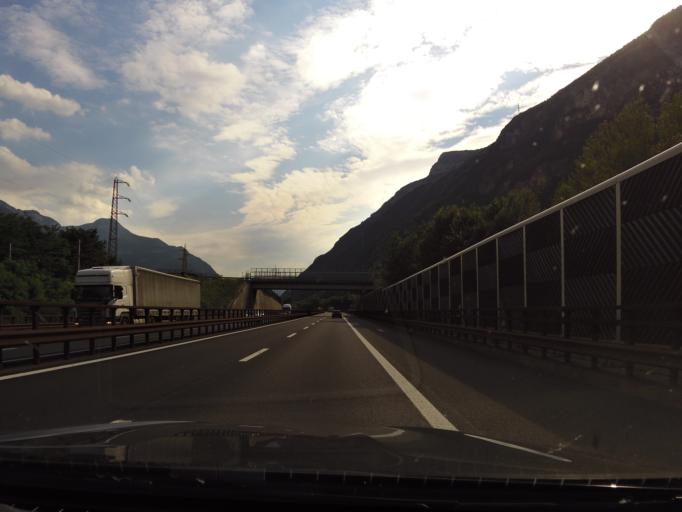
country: IT
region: Trentino-Alto Adige
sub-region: Provincia di Trento
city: Ala
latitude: 45.7662
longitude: 11.0029
